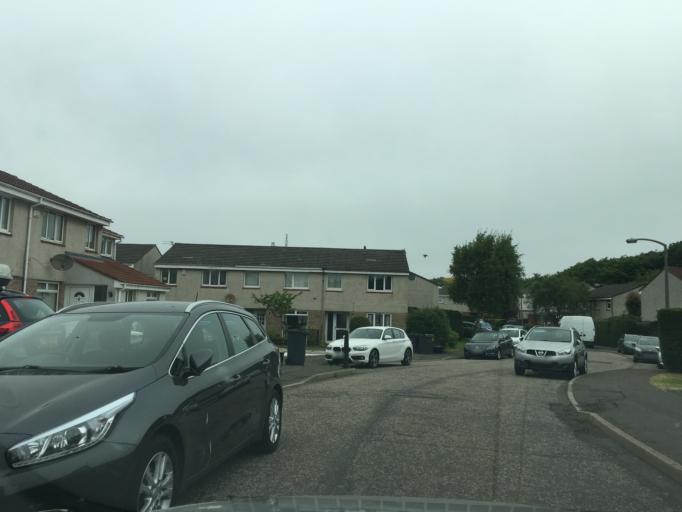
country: GB
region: Scotland
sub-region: Edinburgh
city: Edinburgh
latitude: 55.9069
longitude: -3.1985
